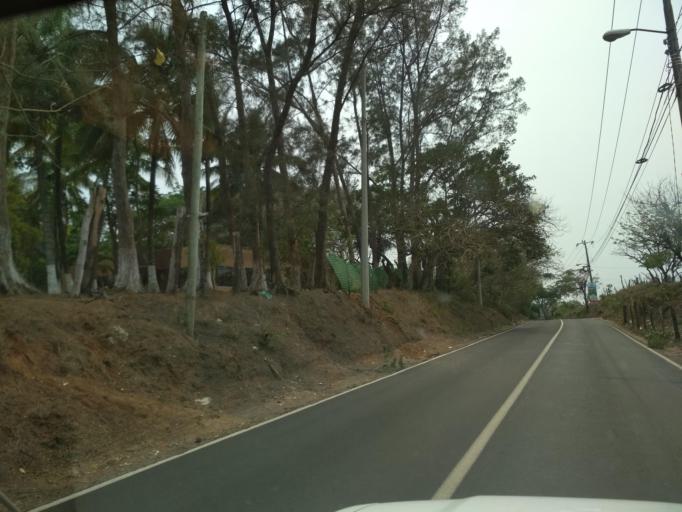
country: MX
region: Veracruz
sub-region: Veracruz
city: Las Amapolas
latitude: 19.1511
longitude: -96.2242
